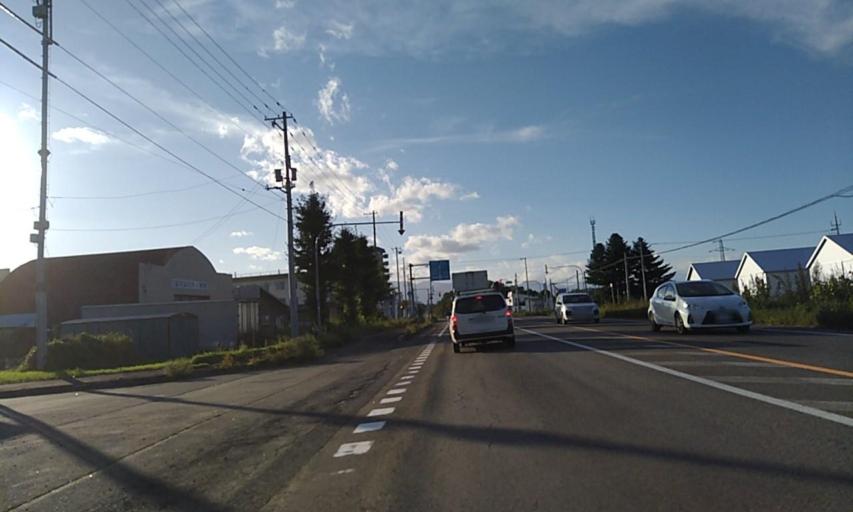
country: JP
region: Hokkaido
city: Otofuke
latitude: 42.9462
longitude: 142.9424
